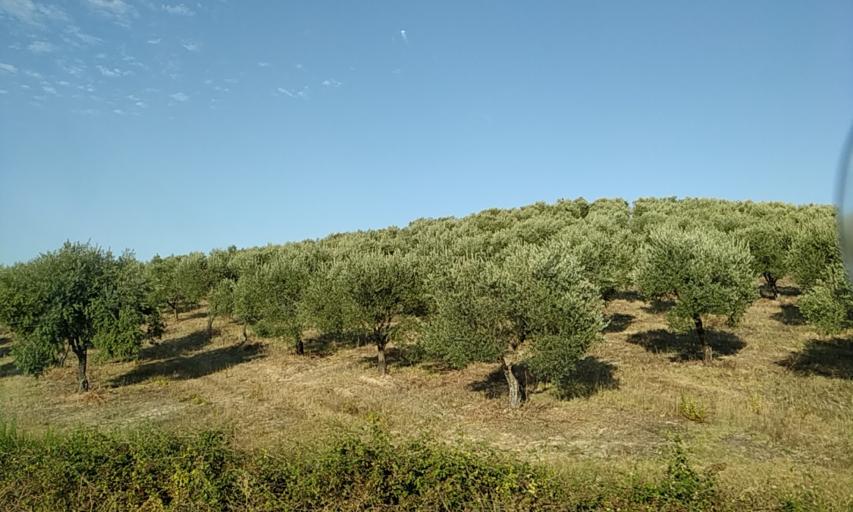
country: PT
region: Santarem
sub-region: Santarem
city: Santarem
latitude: 39.3173
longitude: -8.6701
